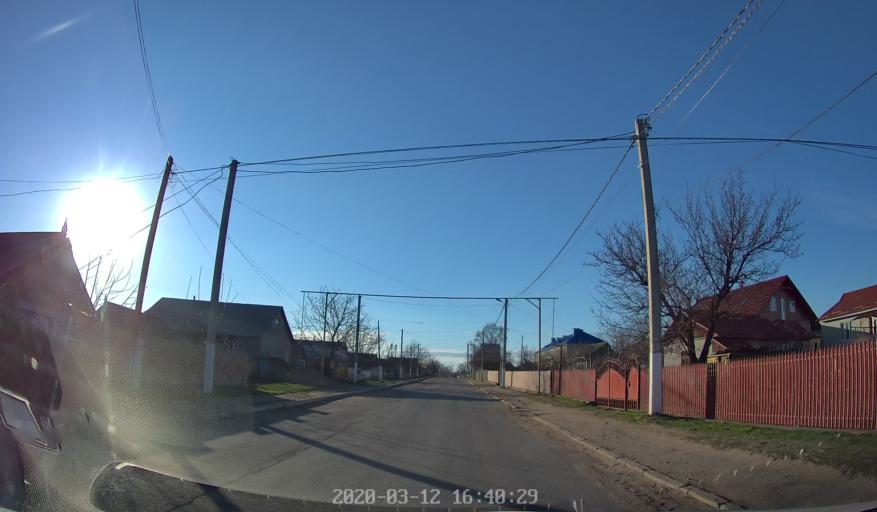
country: MD
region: Anenii Noi
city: Anenii Noi
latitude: 46.8183
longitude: 29.1474
